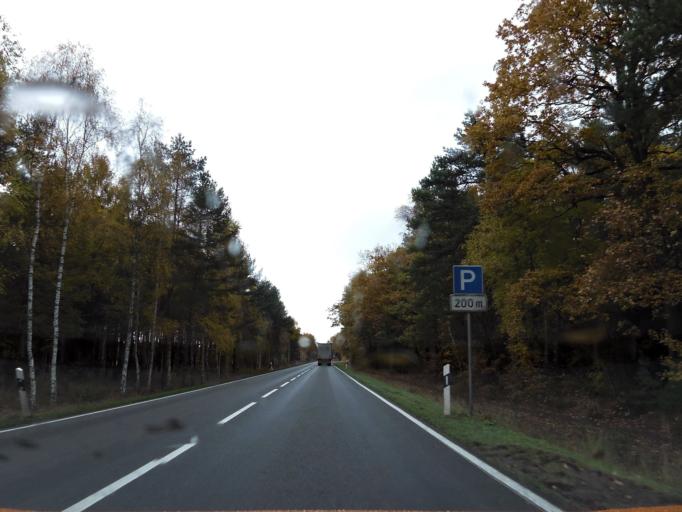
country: DE
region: Saxony-Anhalt
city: Kalbe
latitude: 52.6333
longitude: 11.3068
